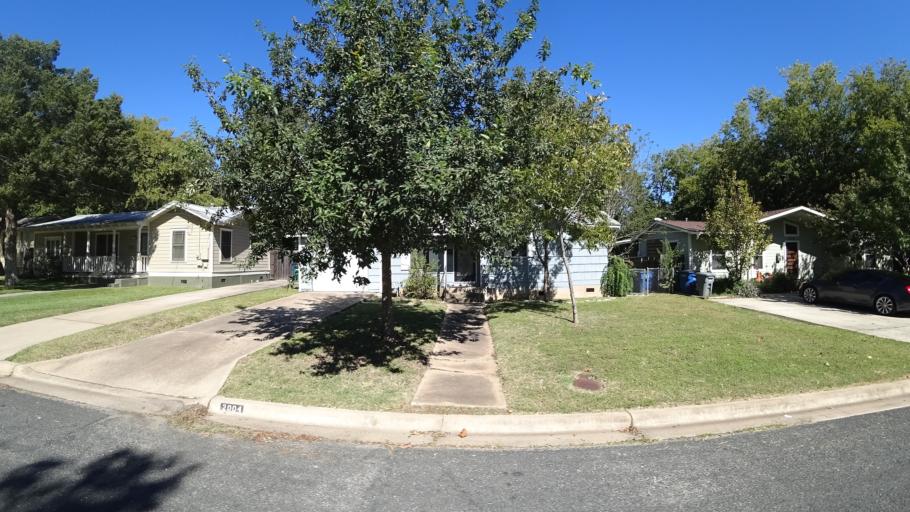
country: US
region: Texas
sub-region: Travis County
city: Austin
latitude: 30.3349
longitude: -97.7379
